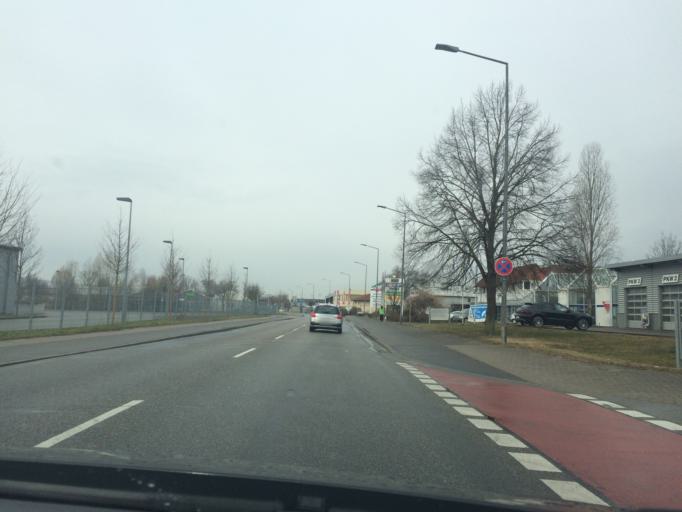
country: DE
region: Rheinland-Pfalz
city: Speyer
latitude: 49.3316
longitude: 8.4495
